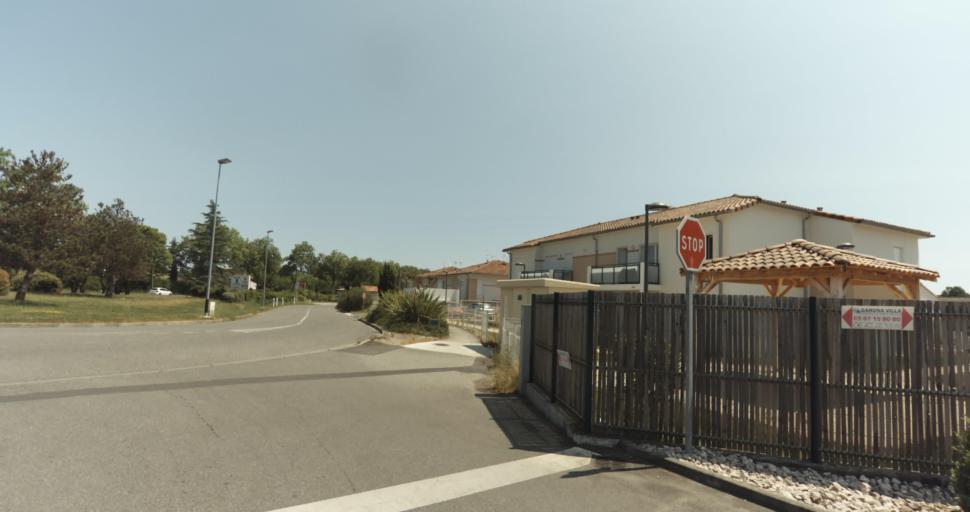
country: FR
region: Midi-Pyrenees
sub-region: Departement de la Haute-Garonne
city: Leguevin
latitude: 43.6004
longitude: 1.2486
